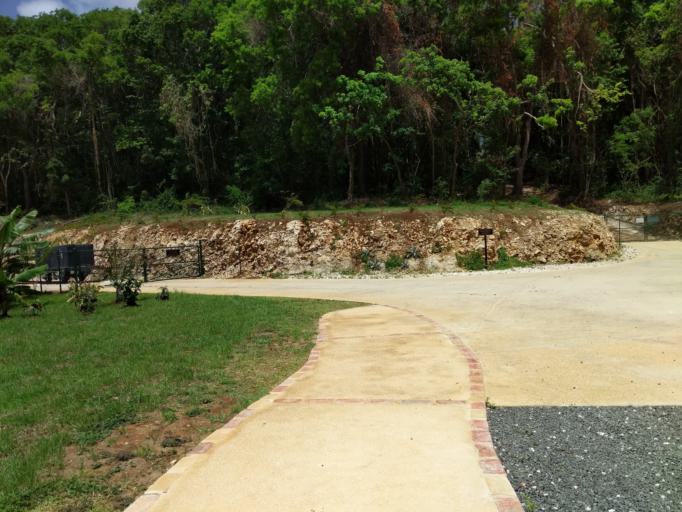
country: BB
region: Saint Andrew
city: Greenland
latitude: 13.2764
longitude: -59.5876
